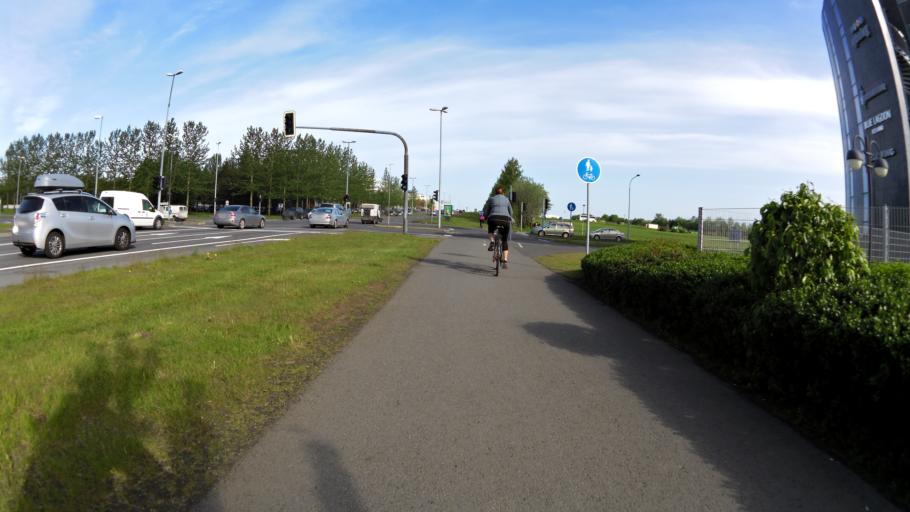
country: IS
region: Capital Region
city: Reykjavik
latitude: 64.1341
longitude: -21.8697
